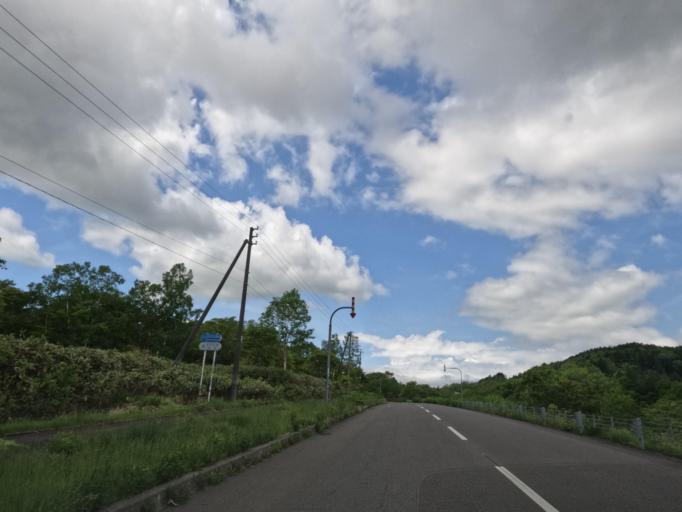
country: JP
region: Hokkaido
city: Tobetsu
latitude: 43.4712
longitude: 141.5965
